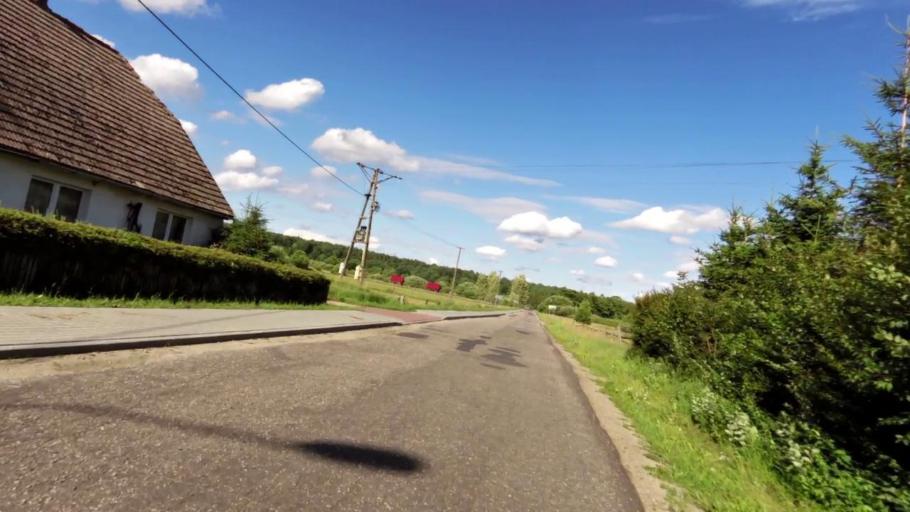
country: PL
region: West Pomeranian Voivodeship
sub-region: Powiat slawienski
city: Slawno
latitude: 54.4361
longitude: 16.7462
